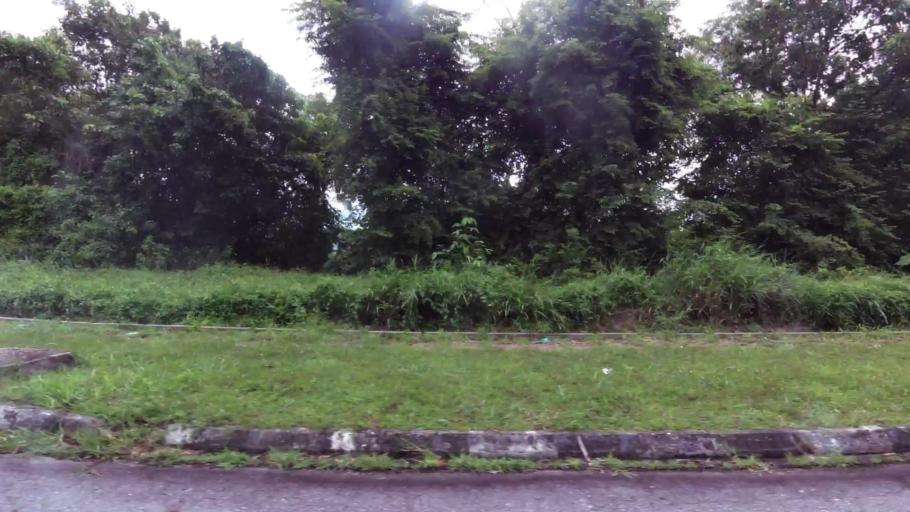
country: BN
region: Brunei and Muara
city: Bandar Seri Begawan
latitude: 4.9023
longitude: 114.9068
